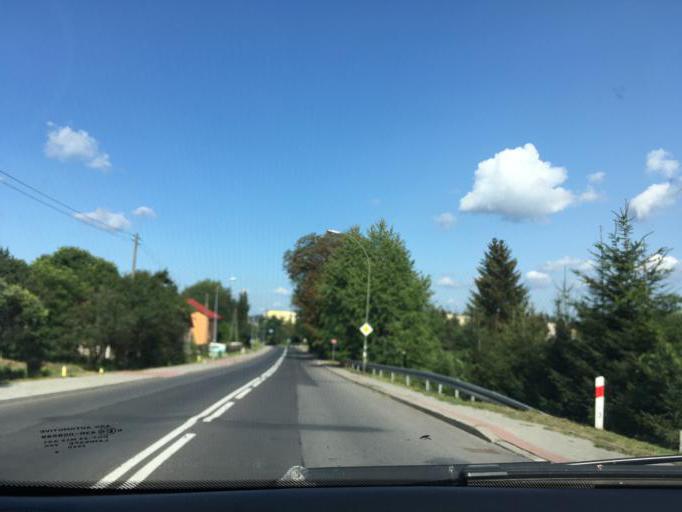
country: PL
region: Subcarpathian Voivodeship
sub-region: Powiat leski
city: Lesko
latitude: 49.4646
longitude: 22.3378
